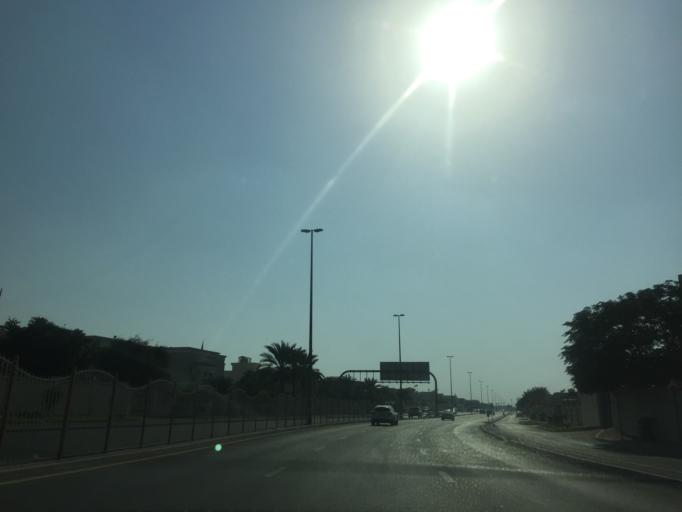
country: AE
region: Dubai
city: Dubai
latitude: 25.1099
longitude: 55.2195
